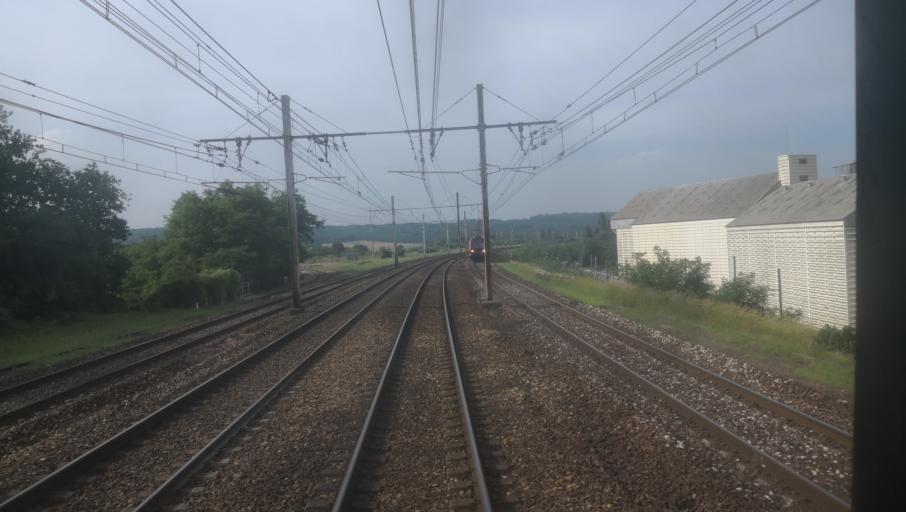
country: FR
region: Ile-de-France
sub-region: Departement de l'Essonne
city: Morigny-Champigny
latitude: 48.4521
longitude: 2.1679
